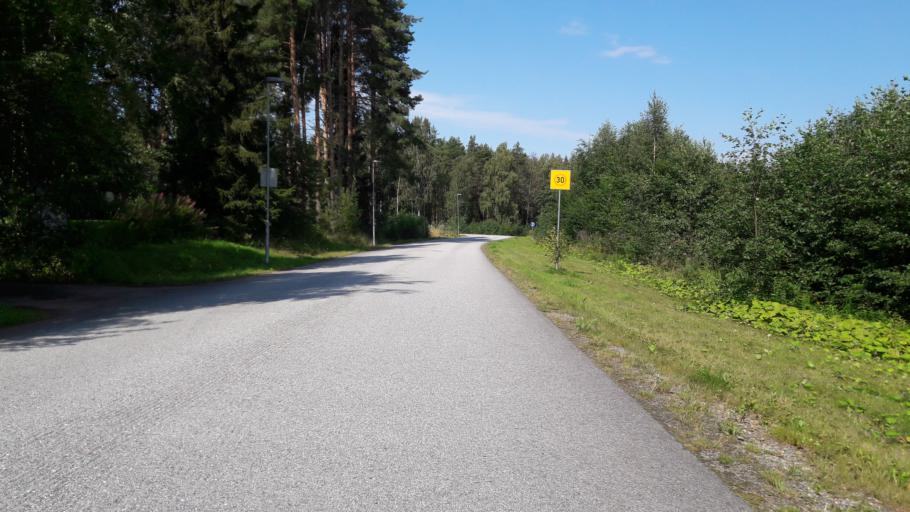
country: FI
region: North Karelia
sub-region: Joensuu
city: Joensuu
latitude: 62.5300
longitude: 29.8506
